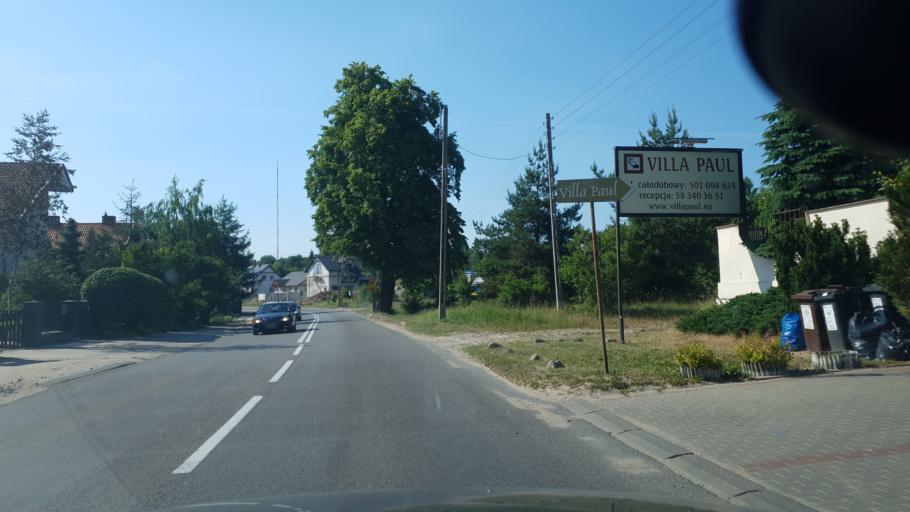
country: PL
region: Pomeranian Voivodeship
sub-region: Powiat kartuski
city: Chwaszczyno
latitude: 54.4408
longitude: 18.4562
